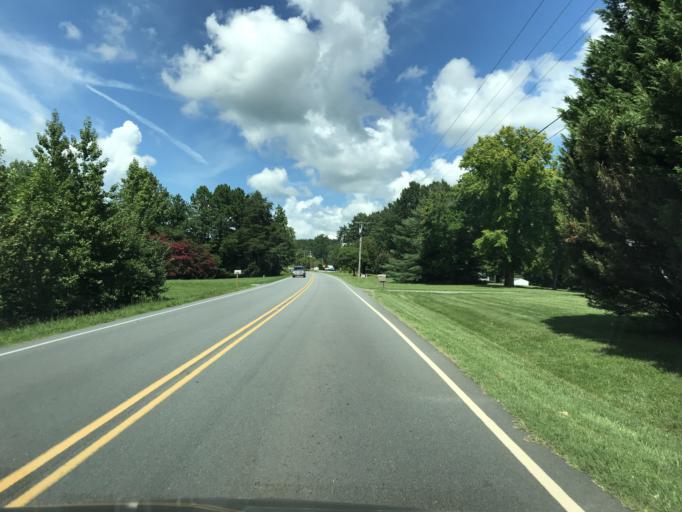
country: US
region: North Carolina
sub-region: Lincoln County
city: Pumpkin Center
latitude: 35.5265
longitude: -81.1344
